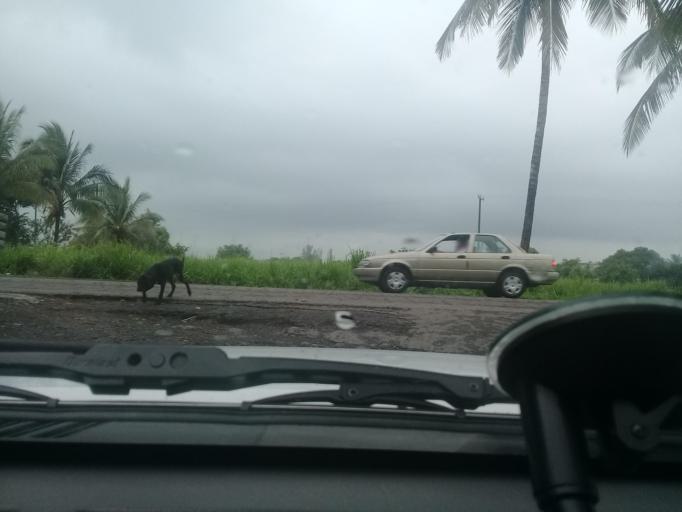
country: MX
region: Veracruz
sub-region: La Antigua
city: Nicolas Blanco (San Pancho)
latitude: 19.3402
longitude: -96.3613
